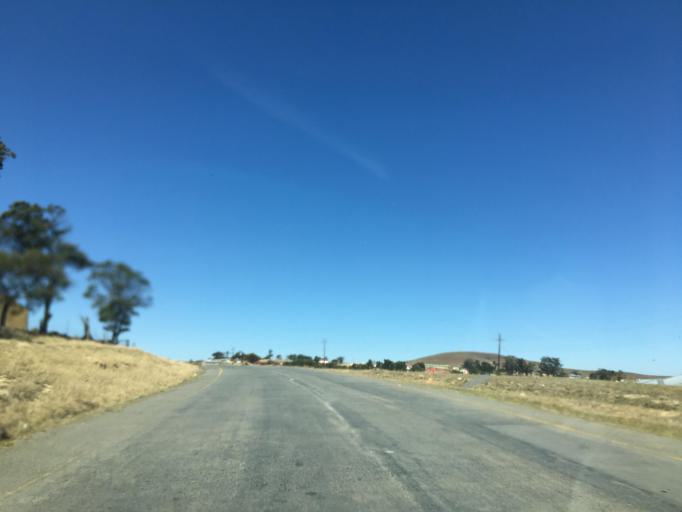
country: ZA
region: Eastern Cape
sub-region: Chris Hani District Municipality
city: Cala
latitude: -31.5537
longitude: 27.8946
